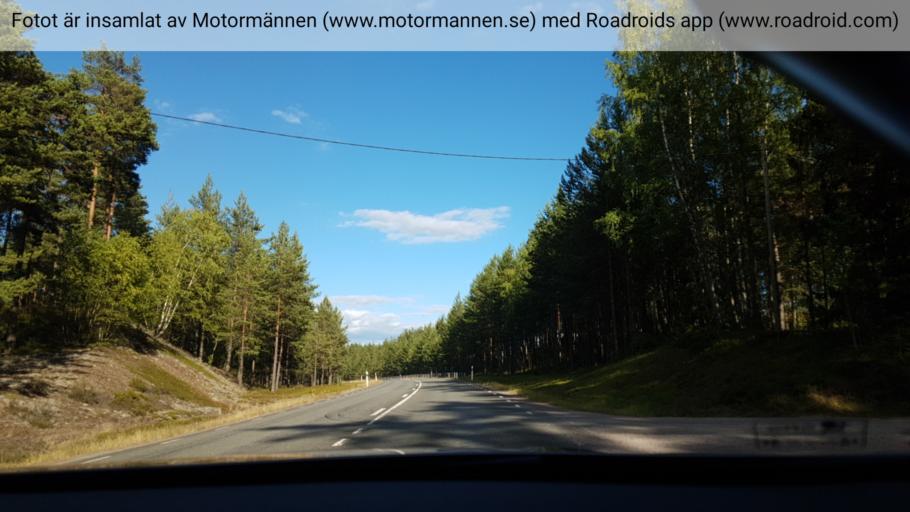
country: SE
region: Vaestra Goetaland
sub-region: Karlsborgs Kommun
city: Molltorp
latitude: 58.4879
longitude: 14.3928
